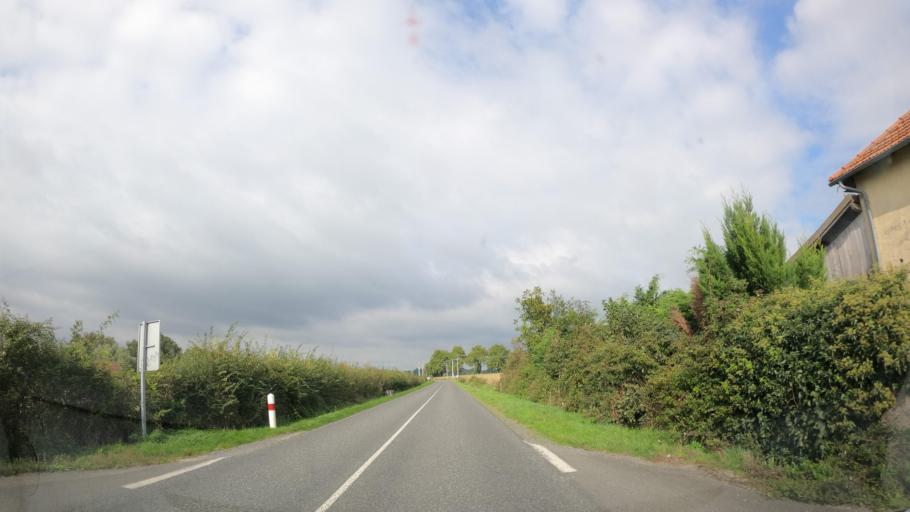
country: FR
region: Auvergne
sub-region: Departement de l'Allier
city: Saint-Gerand-le-Puy
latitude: 46.2408
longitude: 3.5178
